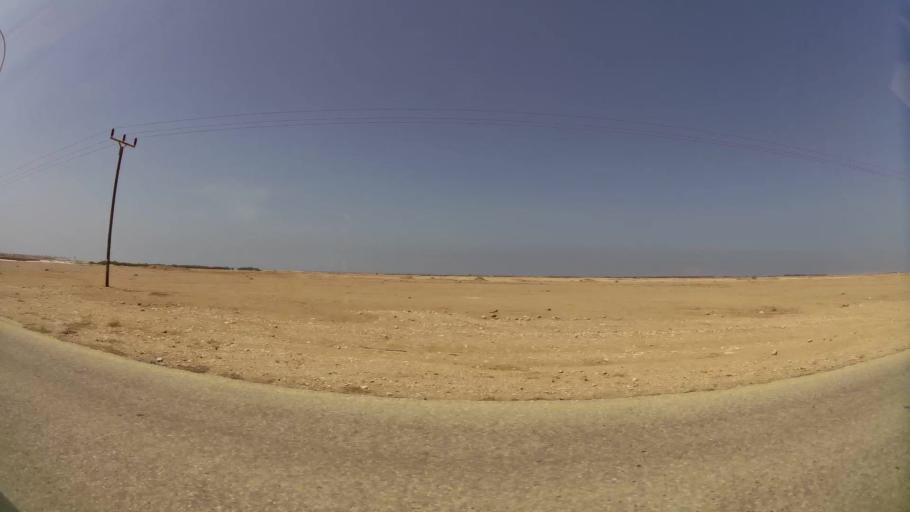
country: OM
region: Zufar
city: Salalah
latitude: 17.0379
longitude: 54.2786
